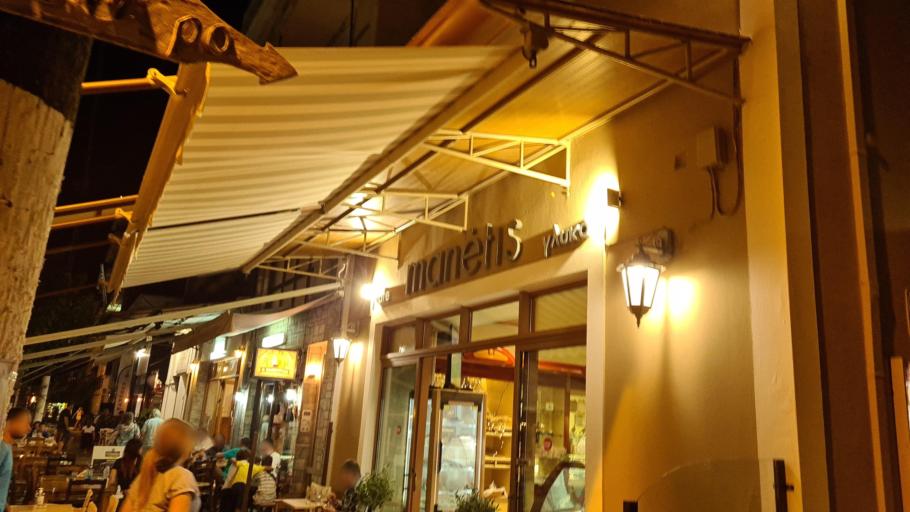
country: GR
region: Central Greece
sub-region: Nomos Evvoias
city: Karystos
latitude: 38.0134
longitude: 24.4192
